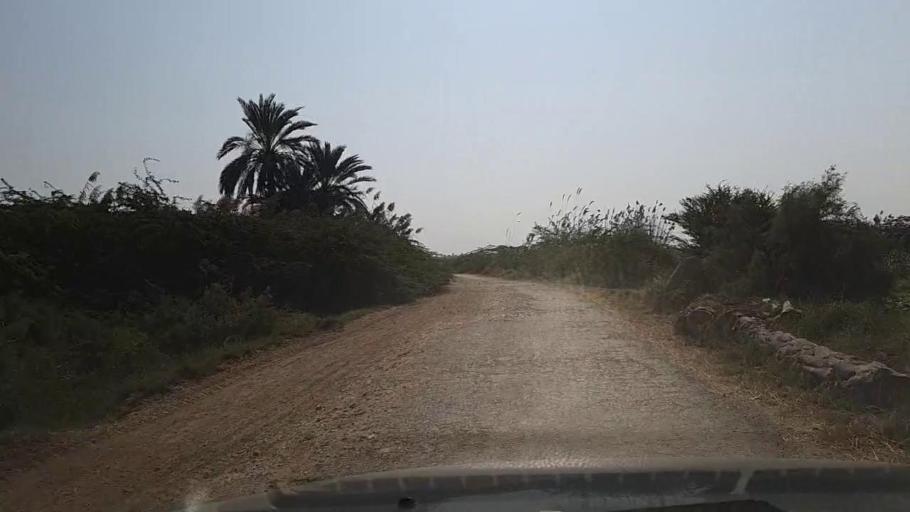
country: PK
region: Sindh
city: Mirpur Sakro
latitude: 24.3918
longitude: 67.6650
